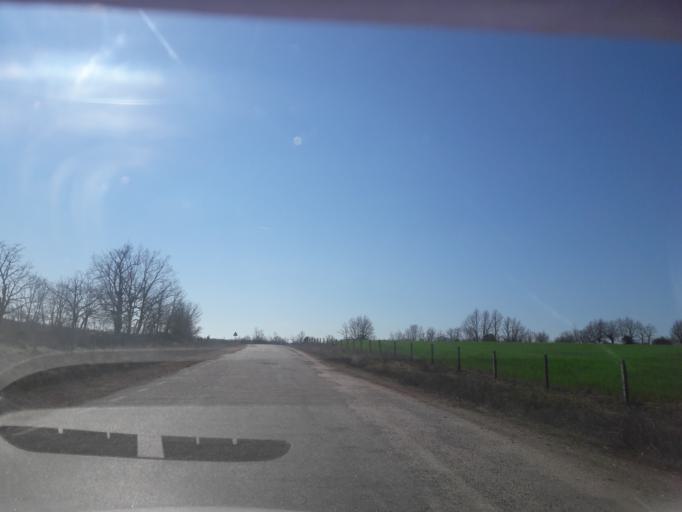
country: ES
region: Castille and Leon
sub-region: Provincia de Salamanca
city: Valsalabroso
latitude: 41.1601
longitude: -6.4952
